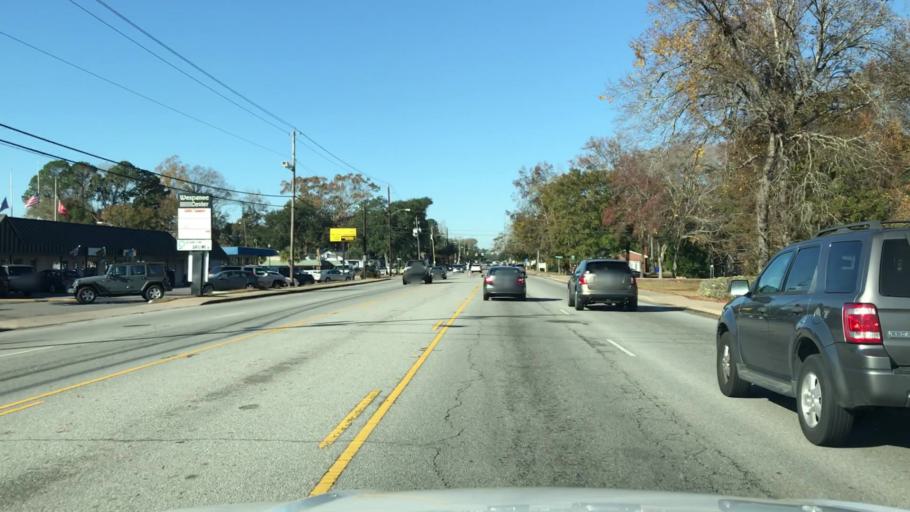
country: US
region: South Carolina
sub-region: Charleston County
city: North Charleston
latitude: 32.7981
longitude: -80.0026
